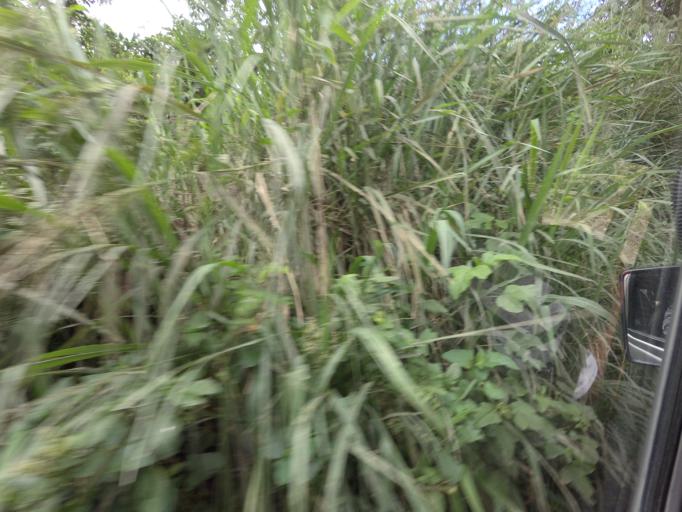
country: CO
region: Huila
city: San Agustin
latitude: 1.9227
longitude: -76.2993
